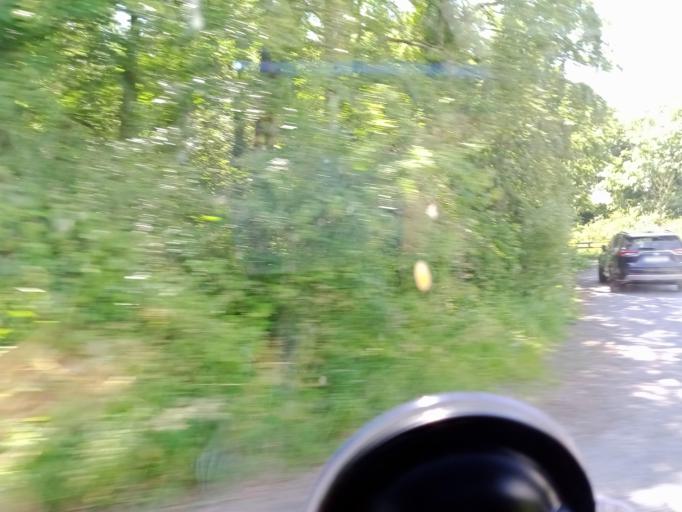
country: IE
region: Leinster
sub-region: Kilkenny
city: Thomastown
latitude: 52.5541
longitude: -7.0953
